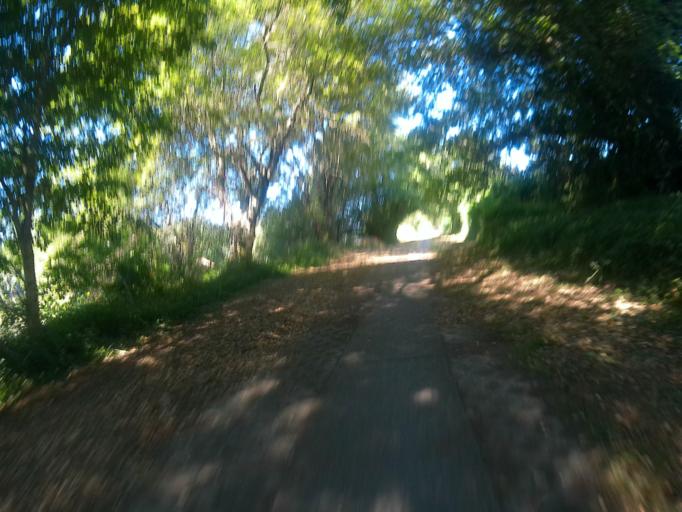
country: PT
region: Viana do Castelo
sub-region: Ponte de Lima
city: Ponte de Lima
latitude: 41.7634
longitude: -8.6032
